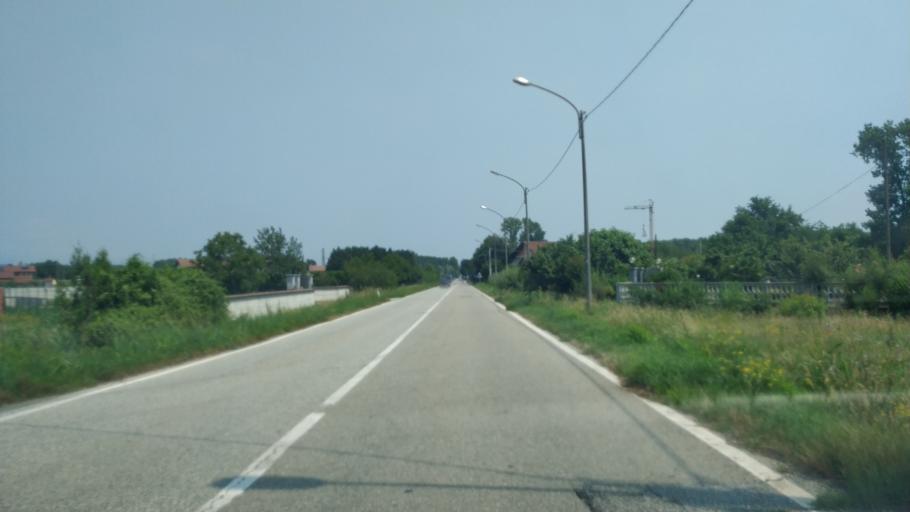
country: IT
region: Piedmont
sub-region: Provincia di Torino
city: Rondissone
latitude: 45.2505
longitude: 7.9659
